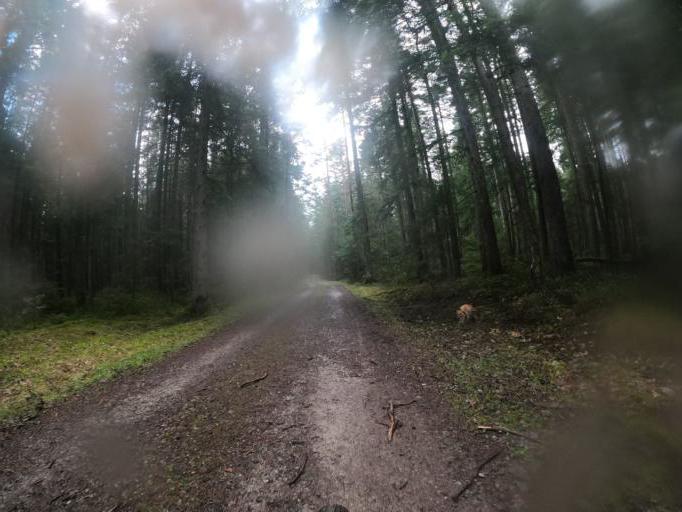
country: DE
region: Baden-Wuerttemberg
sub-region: Karlsruhe Region
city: Oberreichenbach
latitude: 48.7043
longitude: 8.6331
